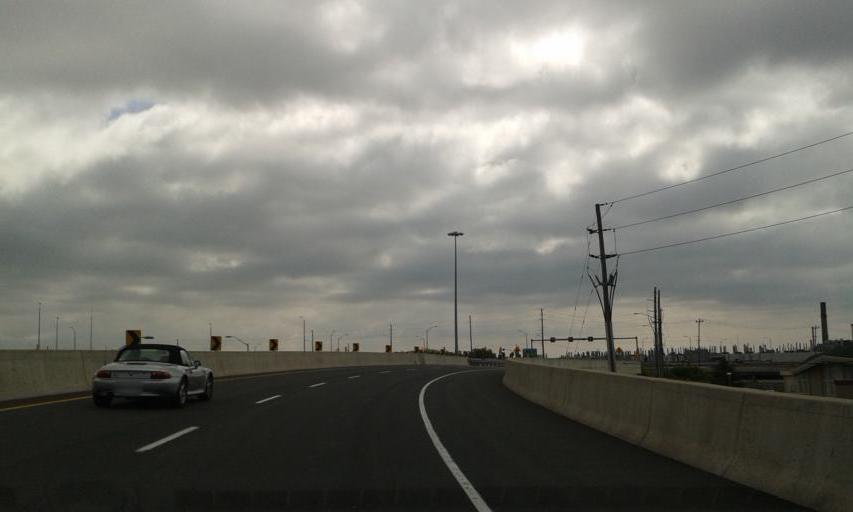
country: CA
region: Ontario
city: Oshawa
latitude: 43.8752
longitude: -78.8782
